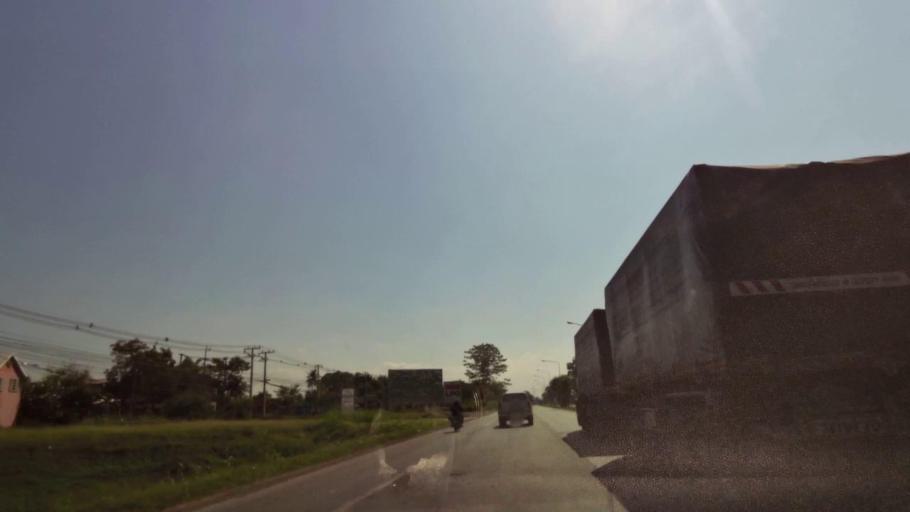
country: TH
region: Nakhon Sawan
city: Nakhon Sawan
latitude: 15.7779
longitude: 100.1213
